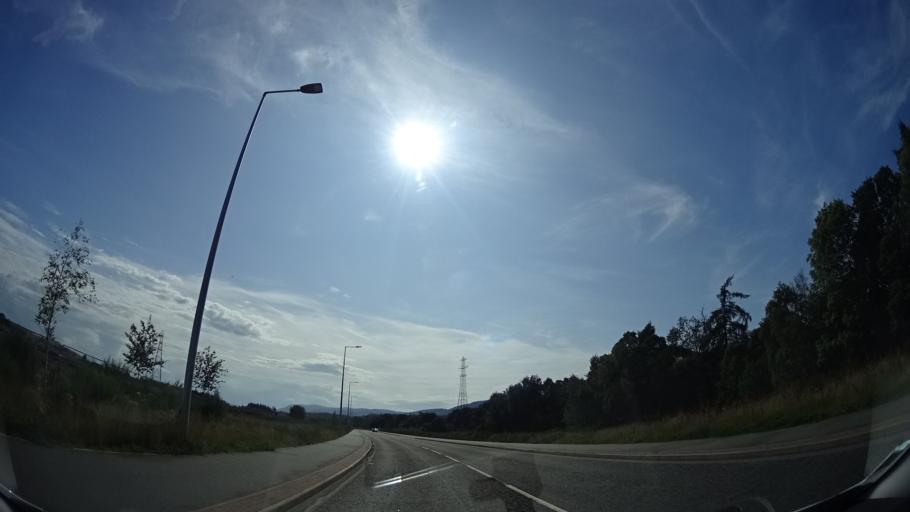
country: GB
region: Scotland
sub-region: Highland
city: Inverness
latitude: 57.4577
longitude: -4.2508
